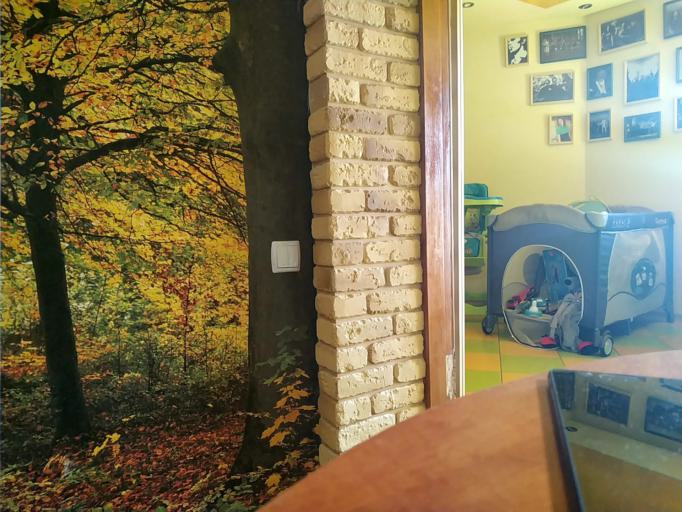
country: RU
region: Tverskaya
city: Vyshniy Volochek
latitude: 57.5078
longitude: 34.6465
